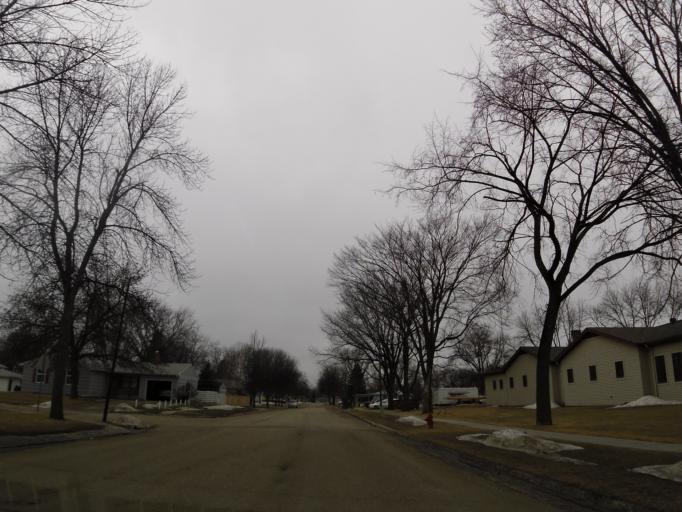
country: US
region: North Dakota
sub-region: Walsh County
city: Grafton
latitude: 48.4105
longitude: -97.4138
